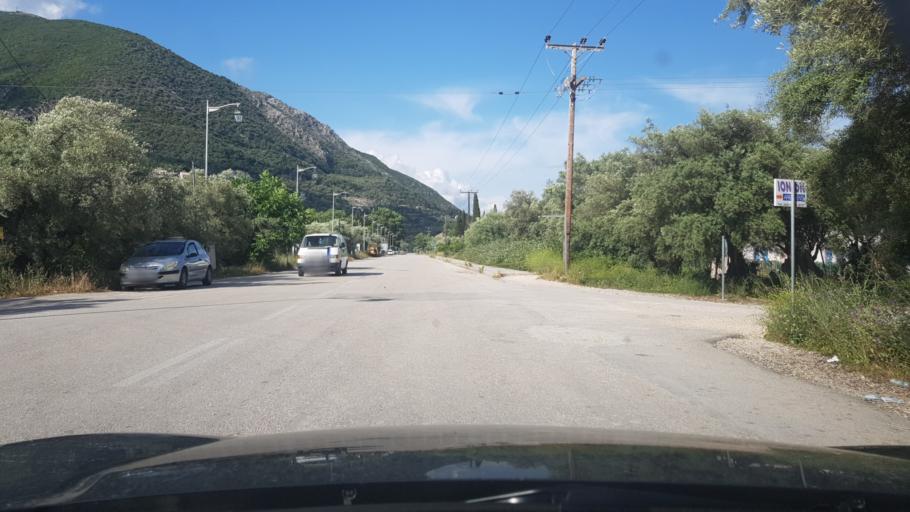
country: GR
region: Ionian Islands
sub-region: Lefkada
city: Nidri
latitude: 38.7099
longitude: 20.7057
